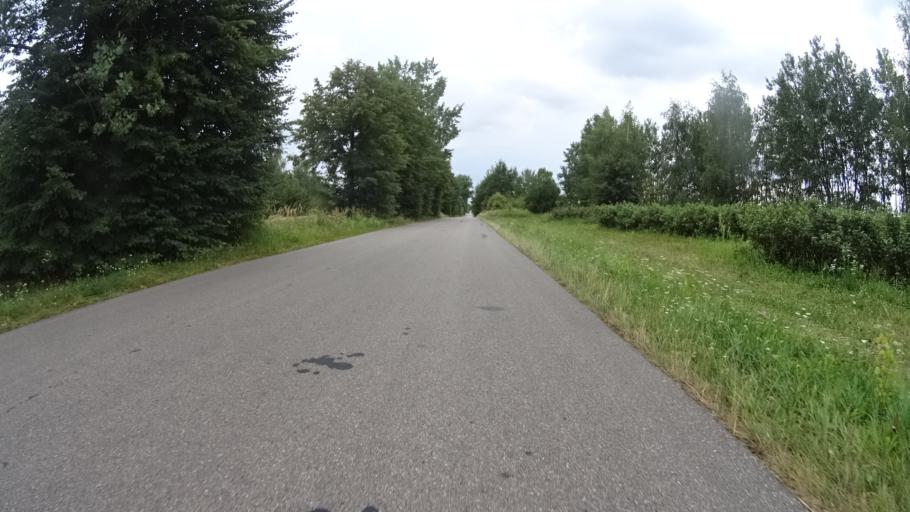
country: PL
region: Masovian Voivodeship
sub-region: Powiat grojecki
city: Goszczyn
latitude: 51.6788
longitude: 20.8597
